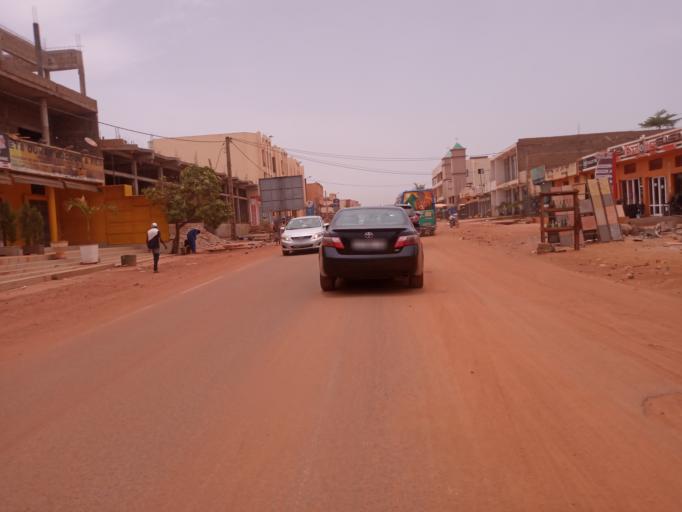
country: ML
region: Bamako
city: Bamako
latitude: 12.5798
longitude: -8.0169
